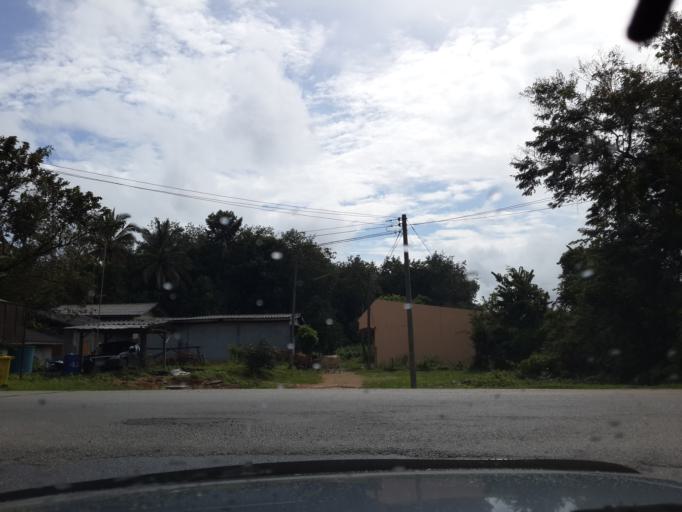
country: TH
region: Narathiwat
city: Rueso
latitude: 6.3851
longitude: 101.5143
